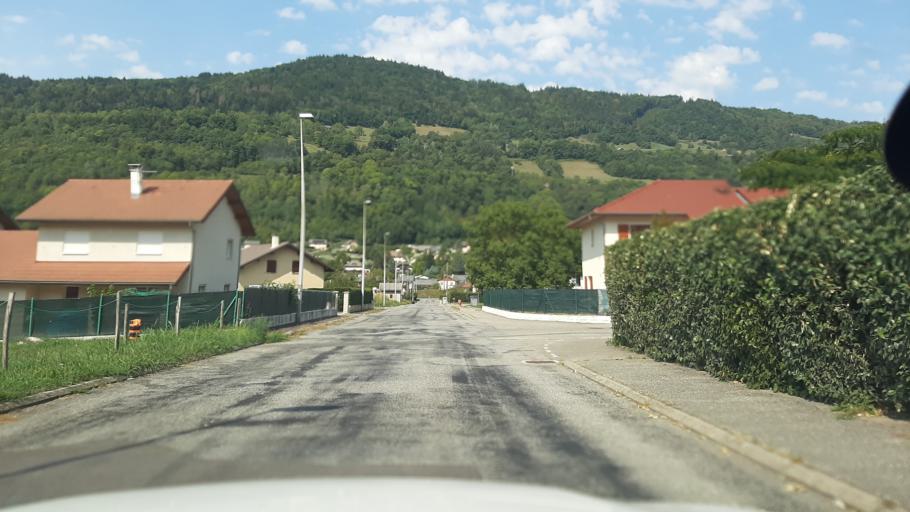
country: FR
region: Rhone-Alpes
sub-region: Departement de la Savoie
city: La Rochette
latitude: 45.4542
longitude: 6.1098
